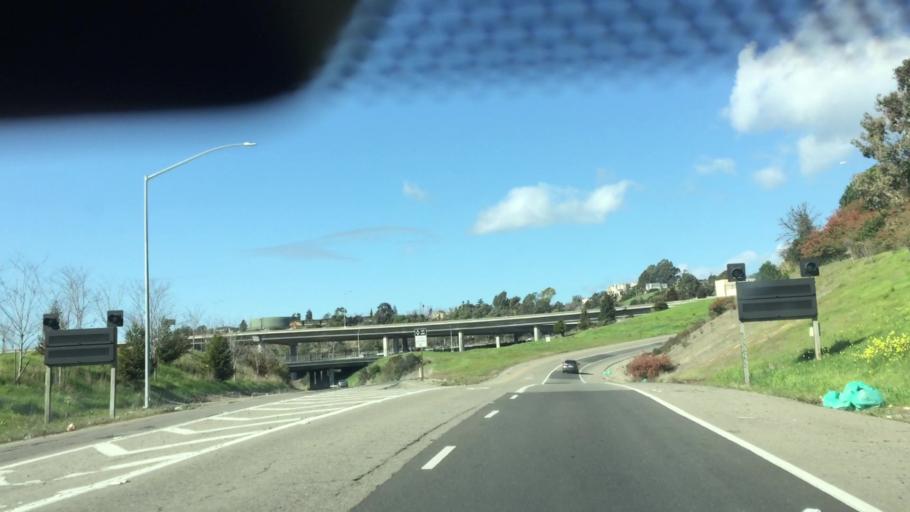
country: US
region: California
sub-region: Alameda County
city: Castro Valley
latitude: 37.6875
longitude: -122.0931
